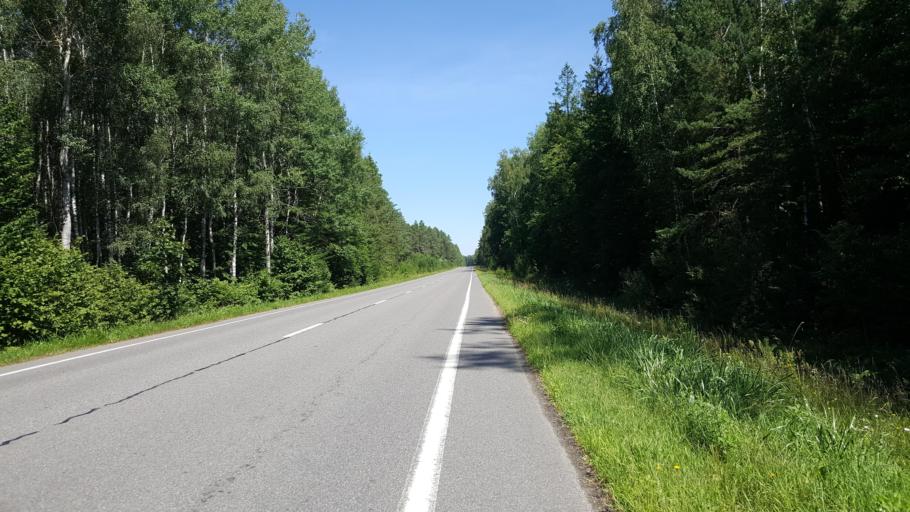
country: BY
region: Brest
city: Pruzhany
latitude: 52.5027
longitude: 24.1757
